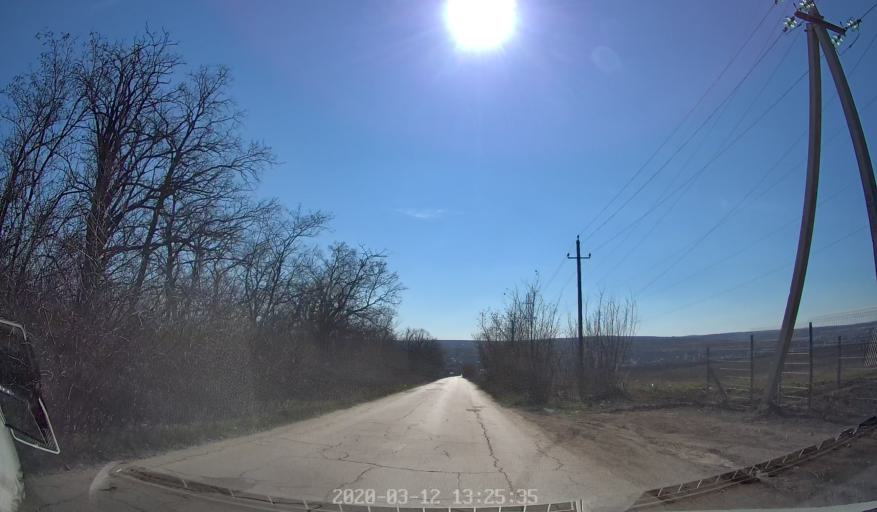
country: MD
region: Laloveni
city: Ialoveni
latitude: 46.9418
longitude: 28.8189
